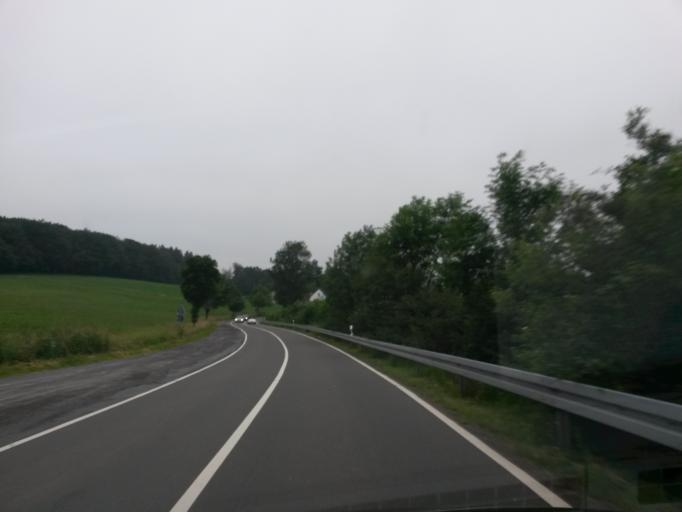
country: DE
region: North Rhine-Westphalia
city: Meinerzhagen
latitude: 51.1133
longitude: 7.6233
